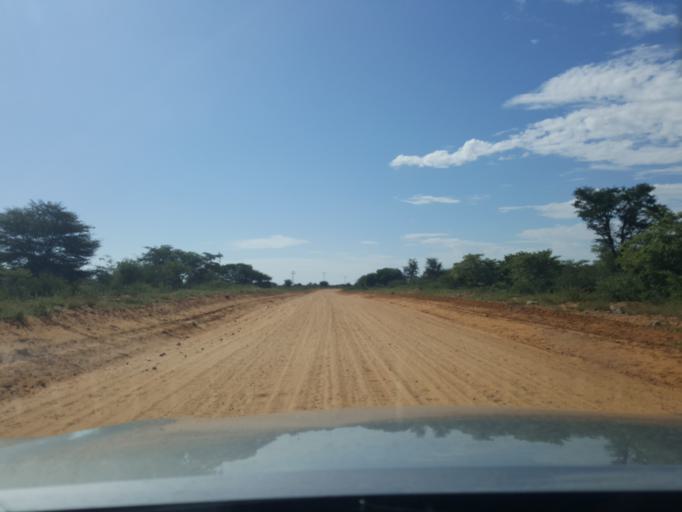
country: BW
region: Kweneng
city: Khudumelapye
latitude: -23.7032
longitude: 24.7230
